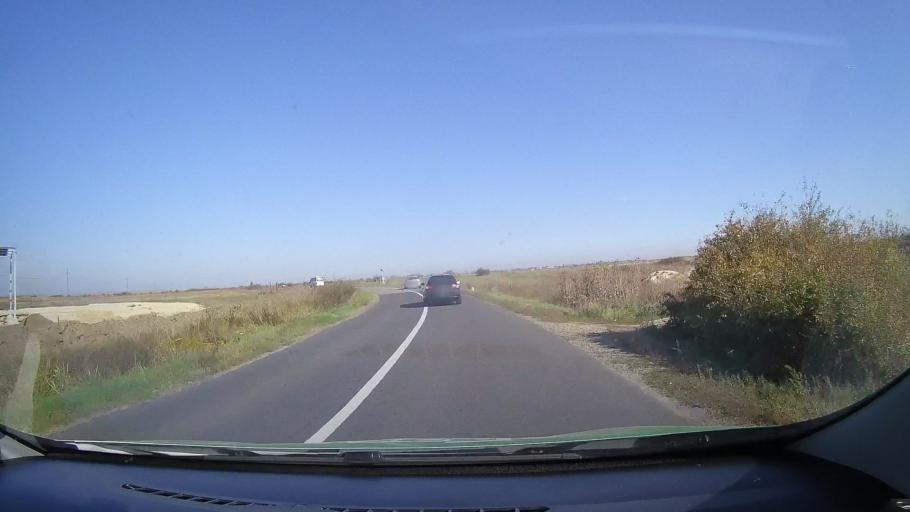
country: RO
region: Satu Mare
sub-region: Comuna Cauas
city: Cauas
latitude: 47.5754
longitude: 22.5499
